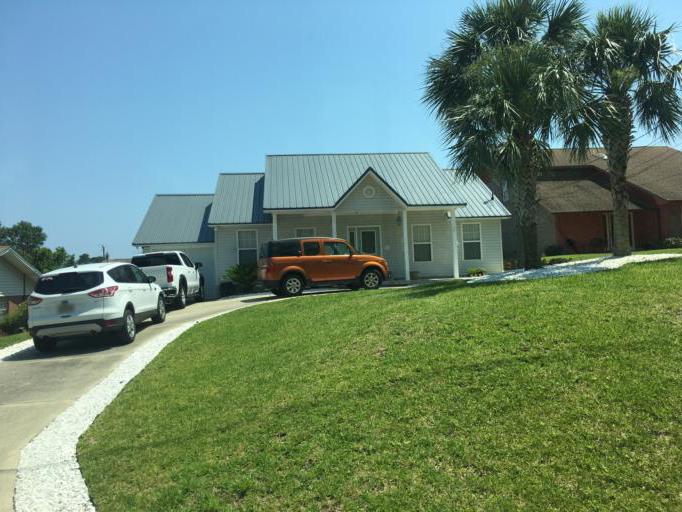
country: US
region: Florida
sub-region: Bay County
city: Laguna Beach
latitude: 30.2253
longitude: -85.8803
